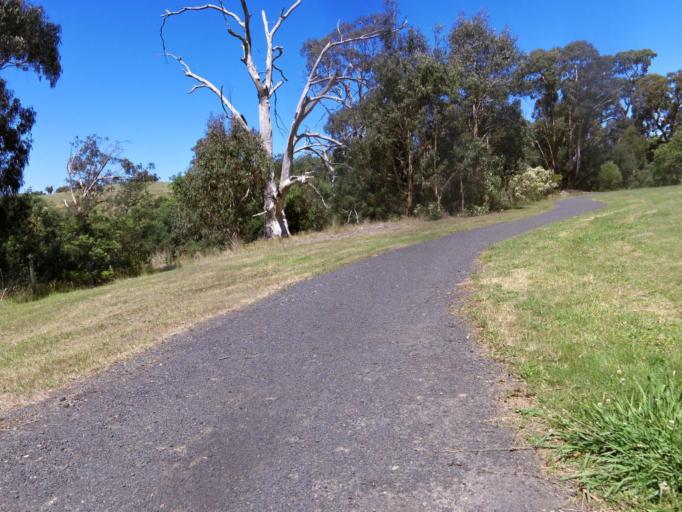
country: AU
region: Victoria
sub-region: Whittlesea
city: Whittlesea
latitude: -37.3557
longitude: 145.0296
